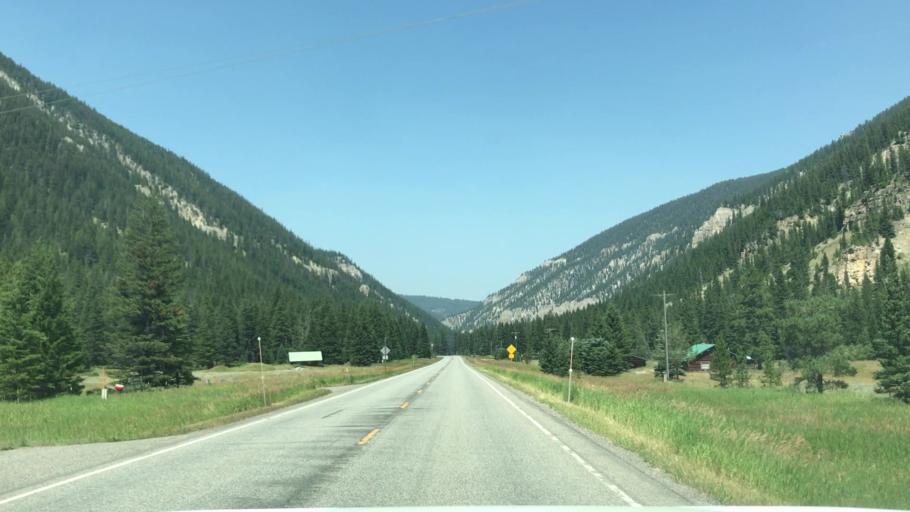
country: US
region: Montana
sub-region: Gallatin County
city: Big Sky
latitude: 45.1208
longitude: -111.2281
